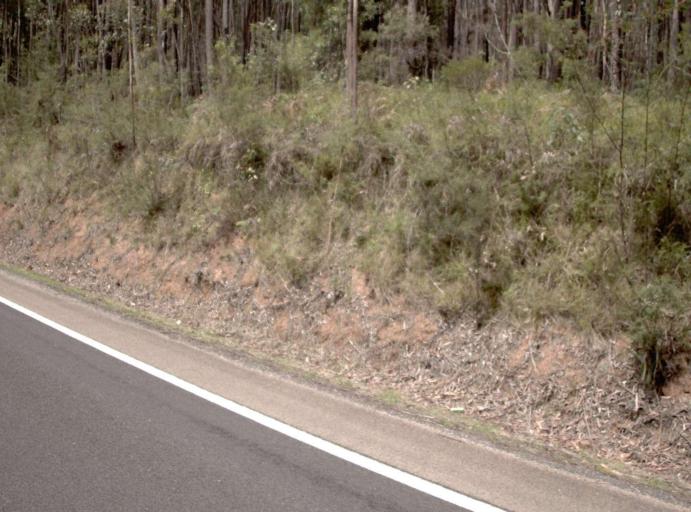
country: AU
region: New South Wales
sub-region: Bombala
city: Bombala
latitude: -37.5443
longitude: 149.3668
